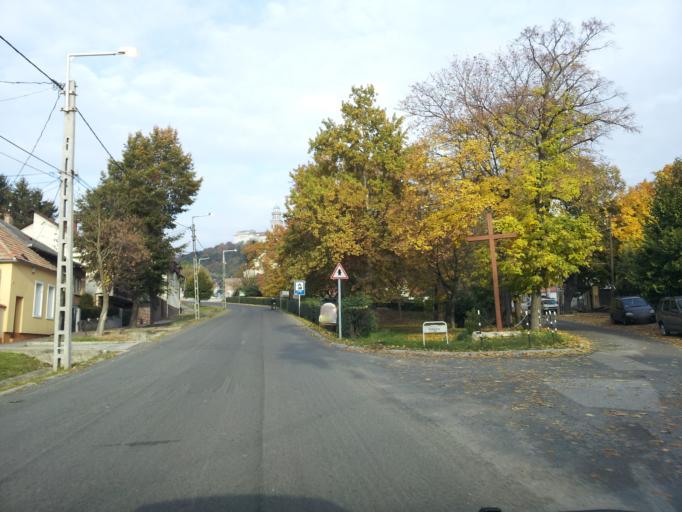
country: HU
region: Gyor-Moson-Sopron
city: Pannonhalma
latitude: 47.5493
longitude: 17.7527
